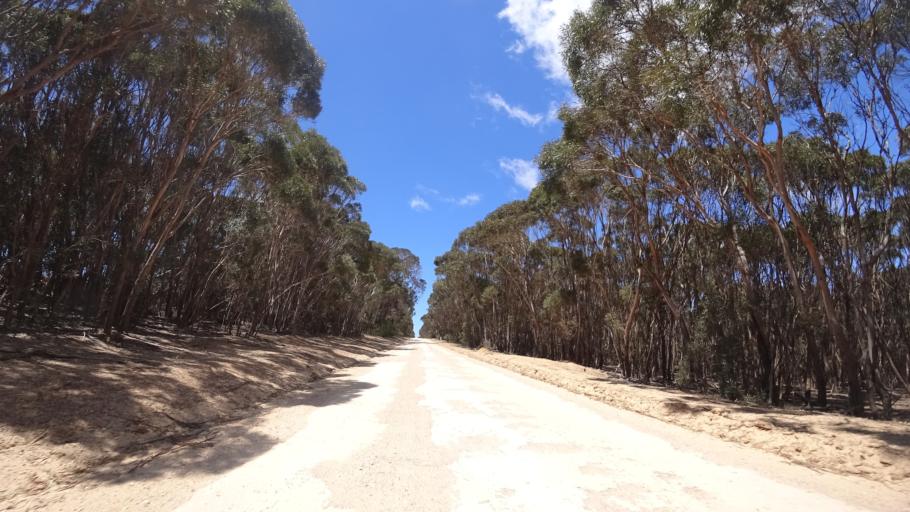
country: AU
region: South Australia
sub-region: Yankalilla
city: Normanville
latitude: -35.8120
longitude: 138.0731
